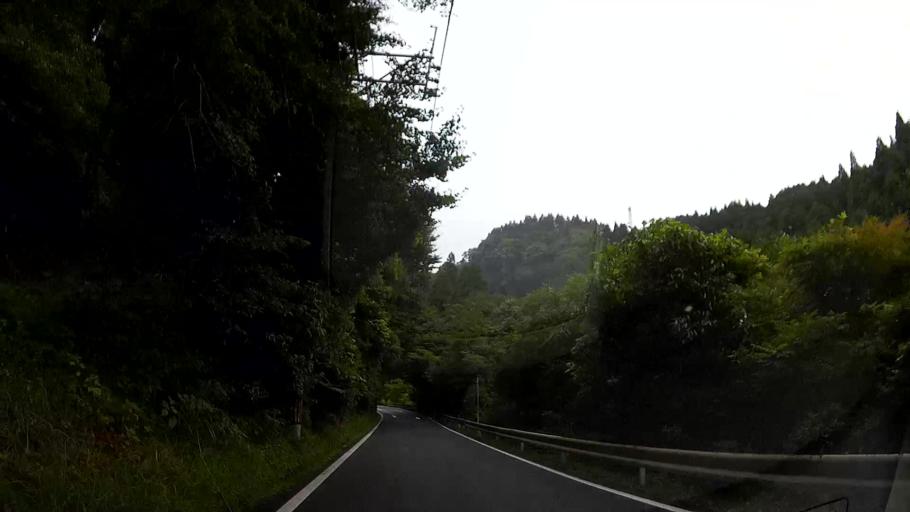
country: JP
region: Kumamoto
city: Kikuchi
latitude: 33.1042
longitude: 130.9609
